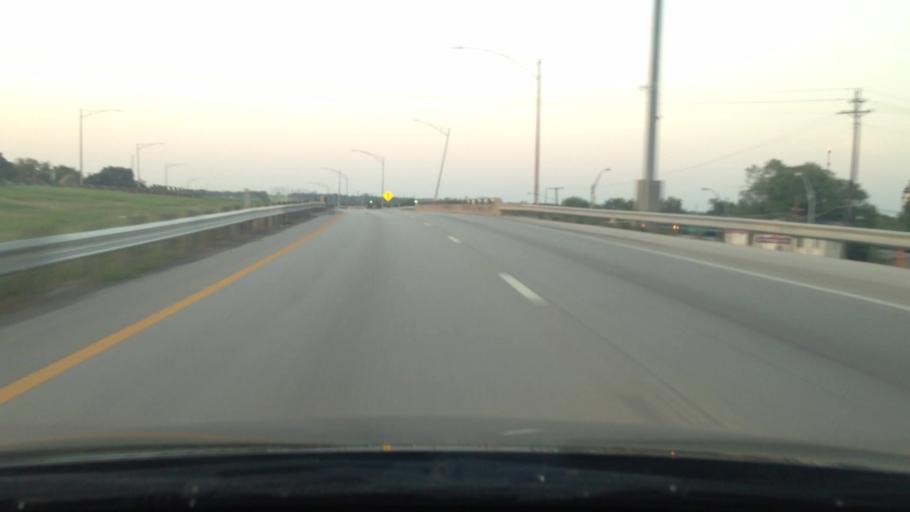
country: US
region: Texas
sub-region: Tarrant County
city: Forest Hill
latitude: 32.7197
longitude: -97.2252
